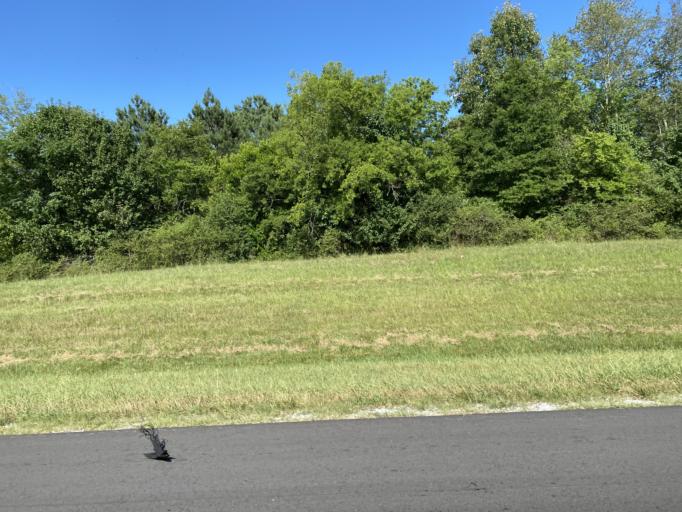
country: US
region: Alabama
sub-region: Limestone County
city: Athens
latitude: 34.7630
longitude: -86.9387
